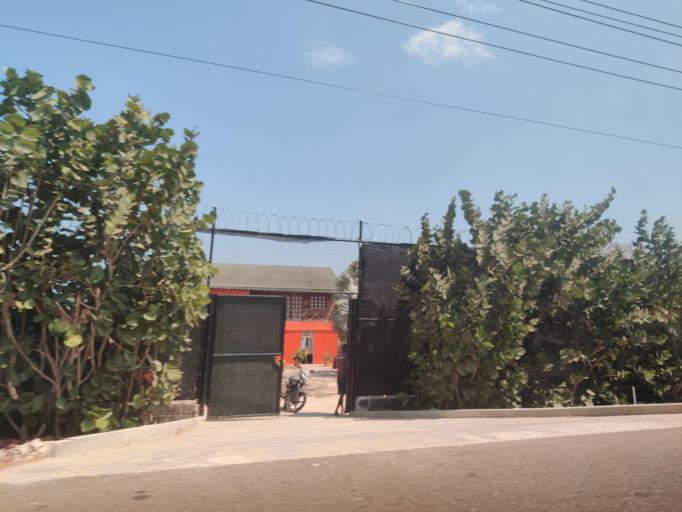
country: CO
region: Bolivar
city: Turbana
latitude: 10.2753
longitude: -75.5436
